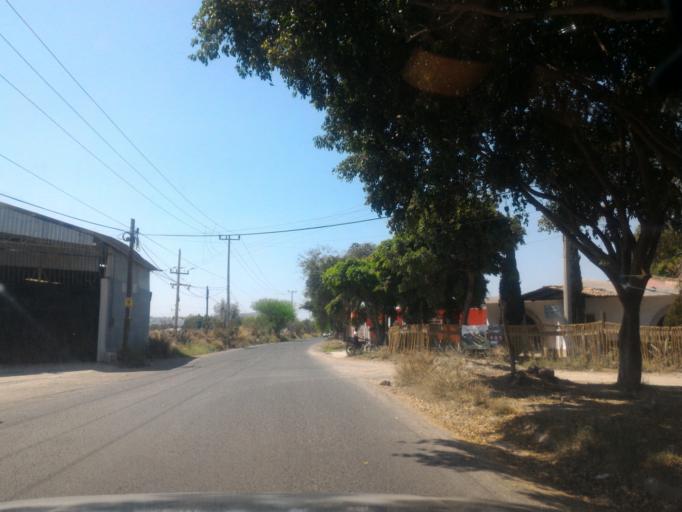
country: MX
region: Jalisco
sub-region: San Pedro Tlaquepaque
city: Santa Anita
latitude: 20.5531
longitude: -103.4316
